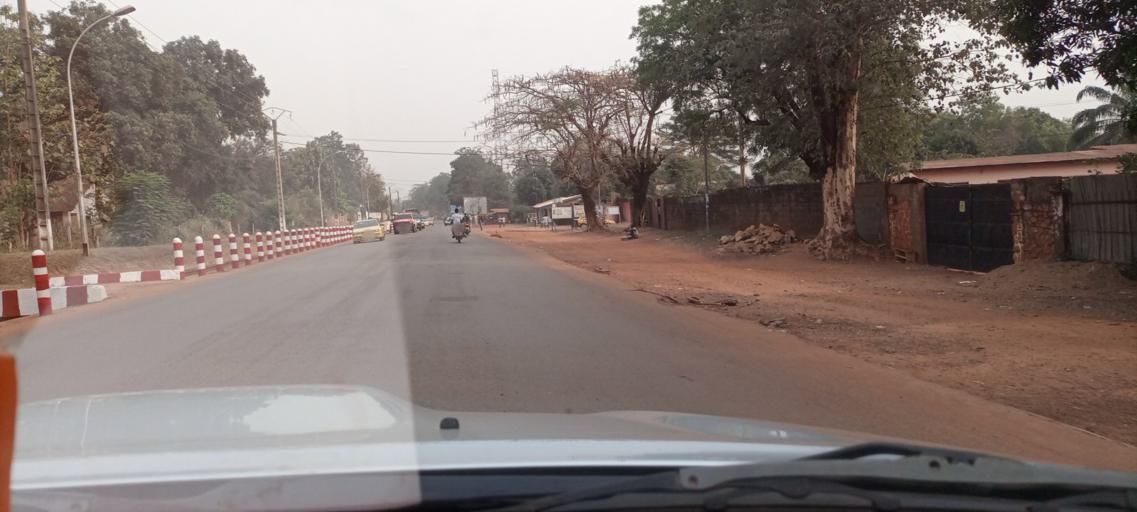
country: CF
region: Bangui
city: Bangui
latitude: 4.3769
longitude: 18.5701
